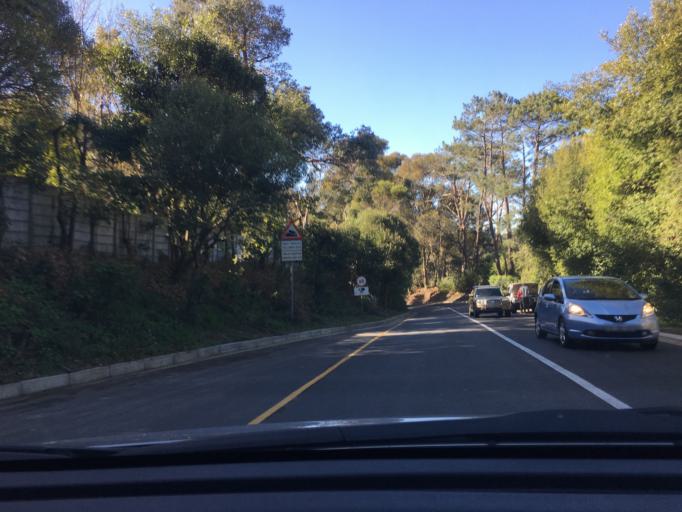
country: ZA
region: Western Cape
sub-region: City of Cape Town
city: Constantia
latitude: -34.0112
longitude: 18.4074
